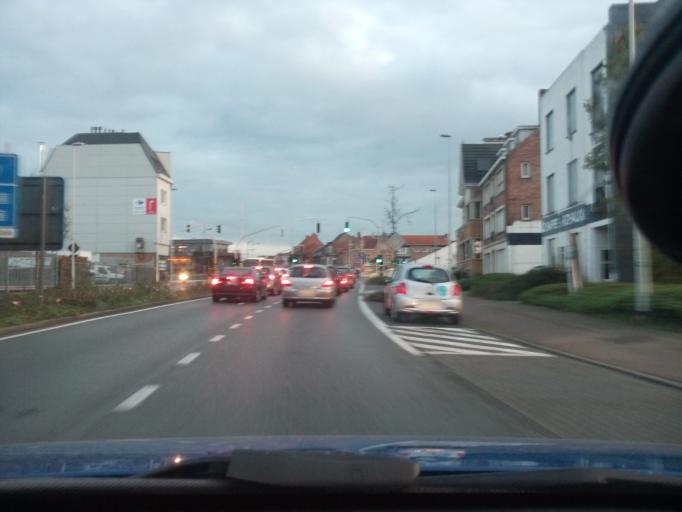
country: BE
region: Flanders
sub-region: Provincie West-Vlaanderen
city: Brugge
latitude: 51.2201
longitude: 3.2086
